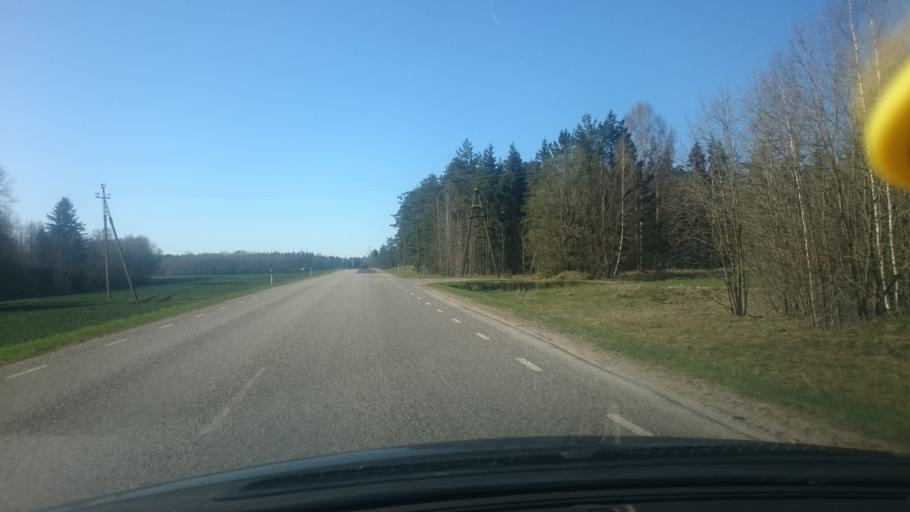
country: EE
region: Harju
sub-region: Raasiku vald
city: Raasiku
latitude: 59.1513
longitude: 25.1956
